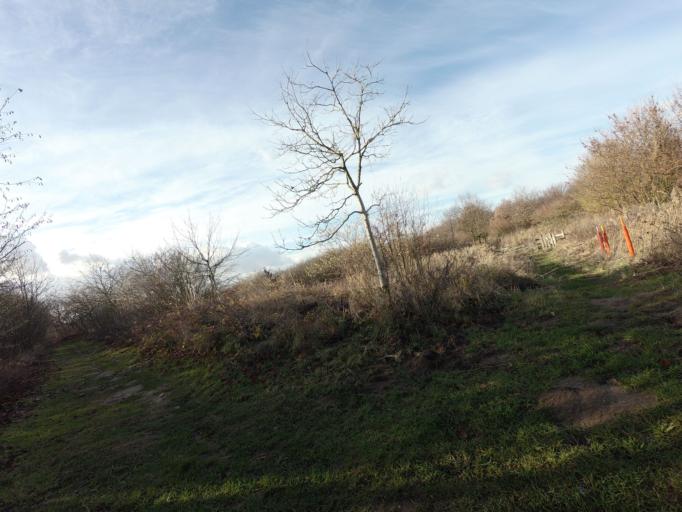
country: BE
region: Flanders
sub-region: Provincie Antwerpen
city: Kapellen
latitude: 51.2789
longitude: 4.4023
